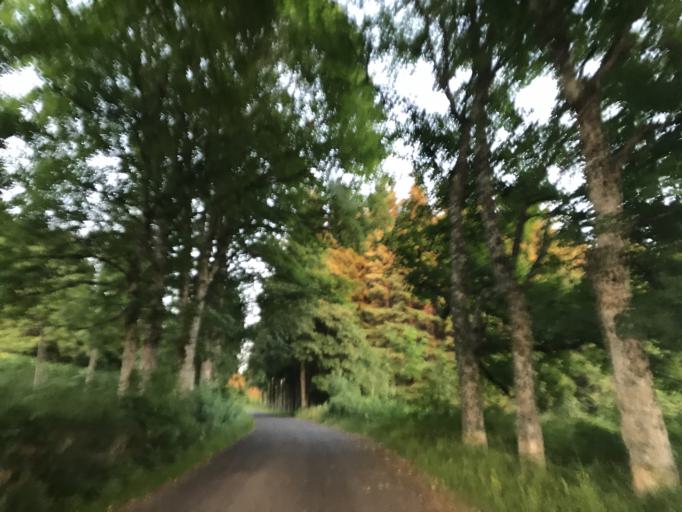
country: FR
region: Rhone-Alpes
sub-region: Departement de la Loire
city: Noiretable
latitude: 45.7663
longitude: 3.7155
